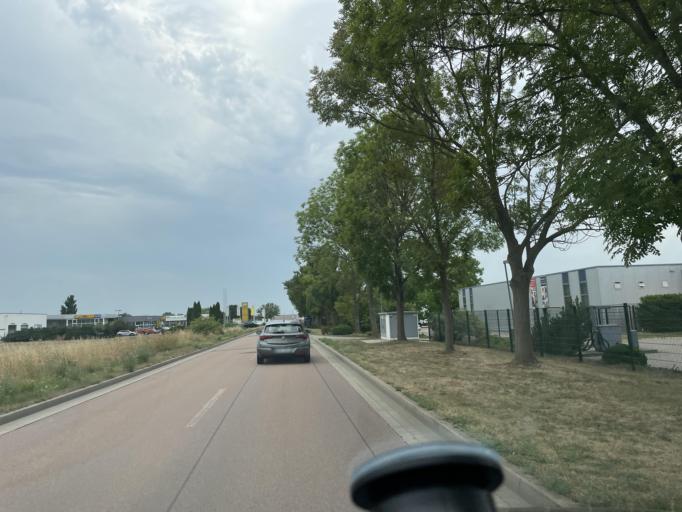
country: DE
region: Saxony-Anhalt
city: Calbe
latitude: 51.8991
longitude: 11.7577
